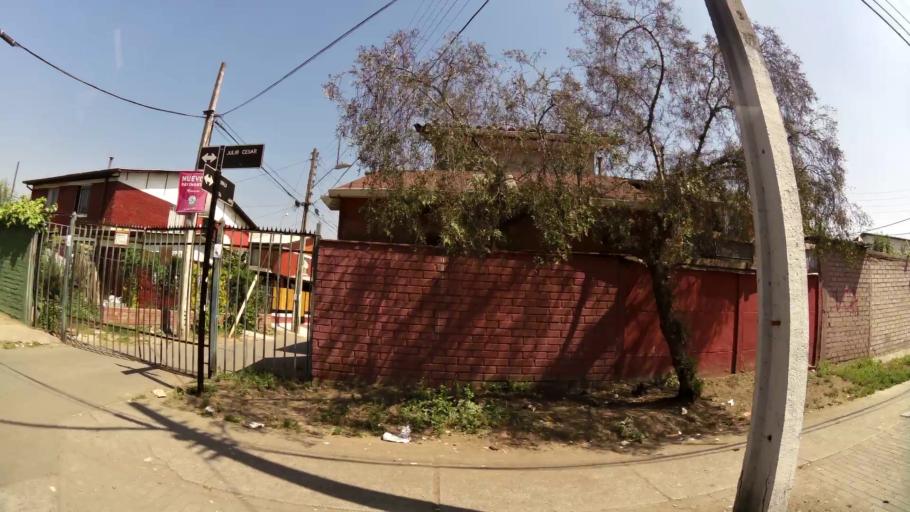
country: CL
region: Santiago Metropolitan
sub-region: Provincia de Santiago
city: La Pintana
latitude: -33.5551
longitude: -70.6071
